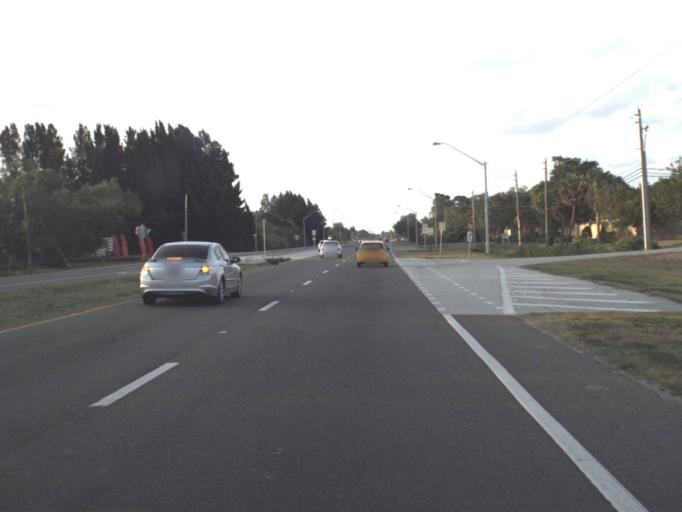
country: US
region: Florida
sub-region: Brevard County
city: Rockledge
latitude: 28.2978
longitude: -80.7428
